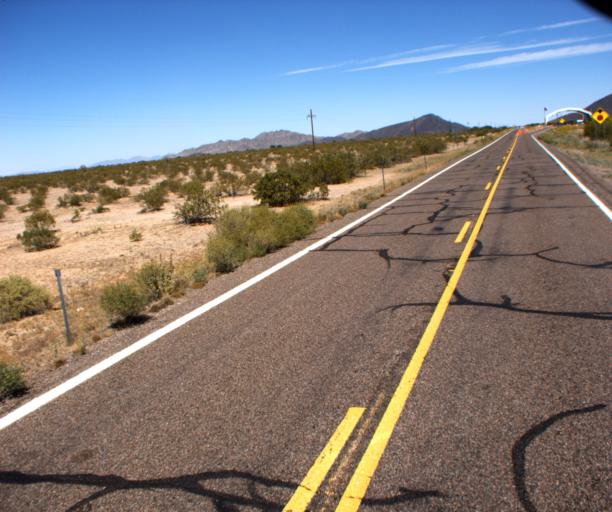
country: US
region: Arizona
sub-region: Maricopa County
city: Gila Bend
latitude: 32.7112
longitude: -112.8439
